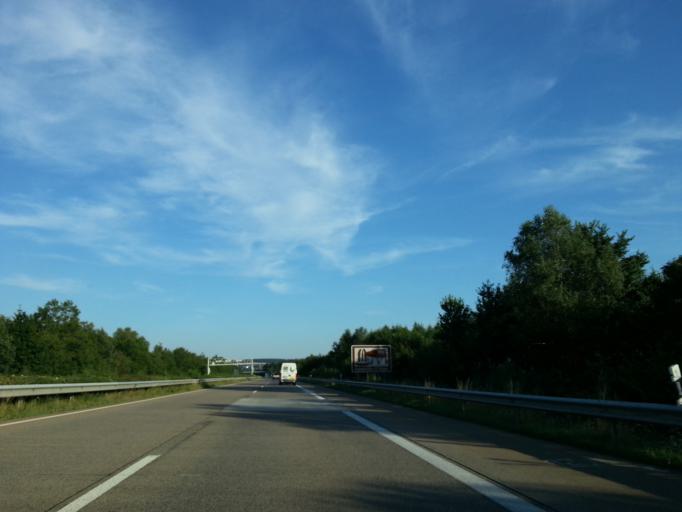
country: DE
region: Rheinland-Pfalz
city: Hinzert-Polert
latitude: 49.6826
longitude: 6.9074
